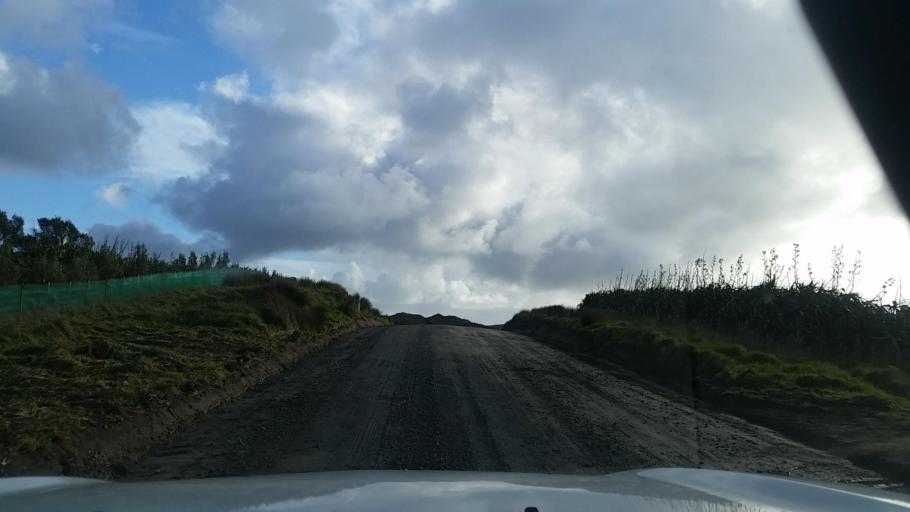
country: NZ
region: Chatham Islands
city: Waitangi
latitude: -43.8093
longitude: -176.5981
